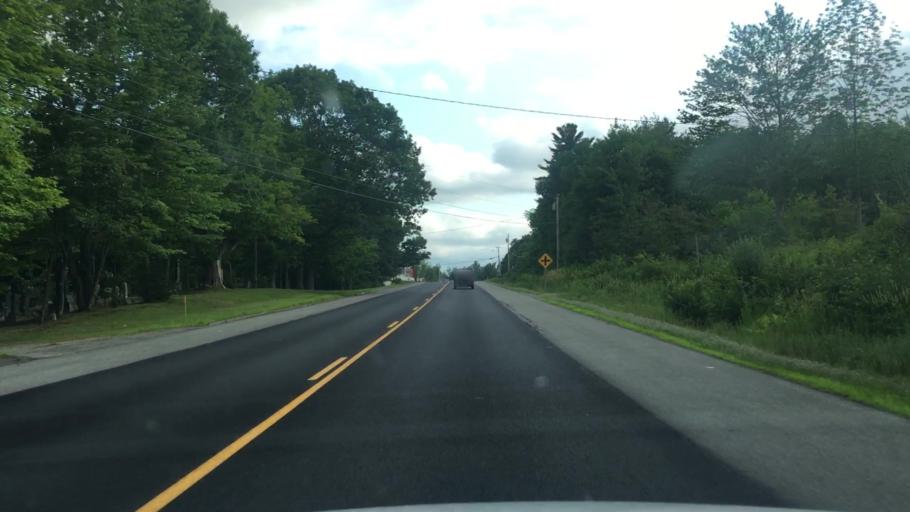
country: US
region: Maine
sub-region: Knox County
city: Washington
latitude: 44.3887
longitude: -69.3568
